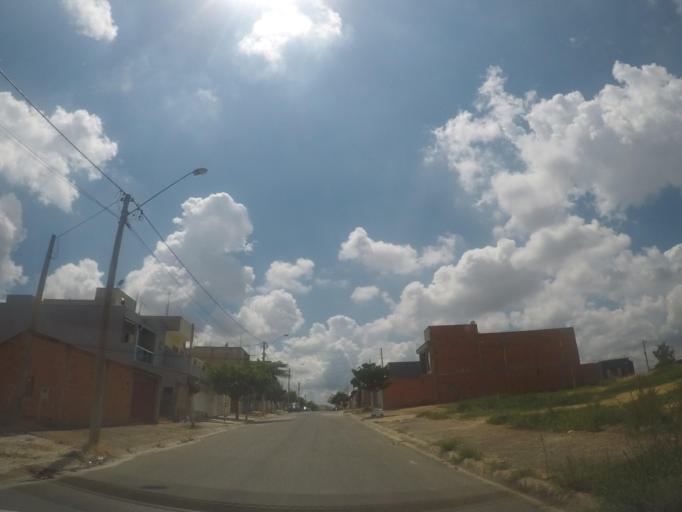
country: BR
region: Sao Paulo
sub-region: Hortolandia
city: Hortolandia
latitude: -22.8393
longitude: -47.2024
